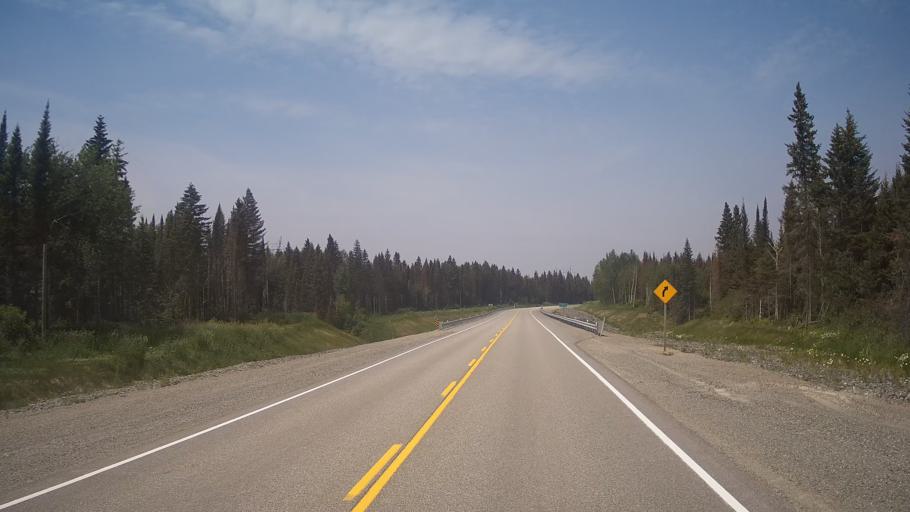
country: CA
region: Ontario
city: Timmins
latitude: 48.7294
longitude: -81.3516
